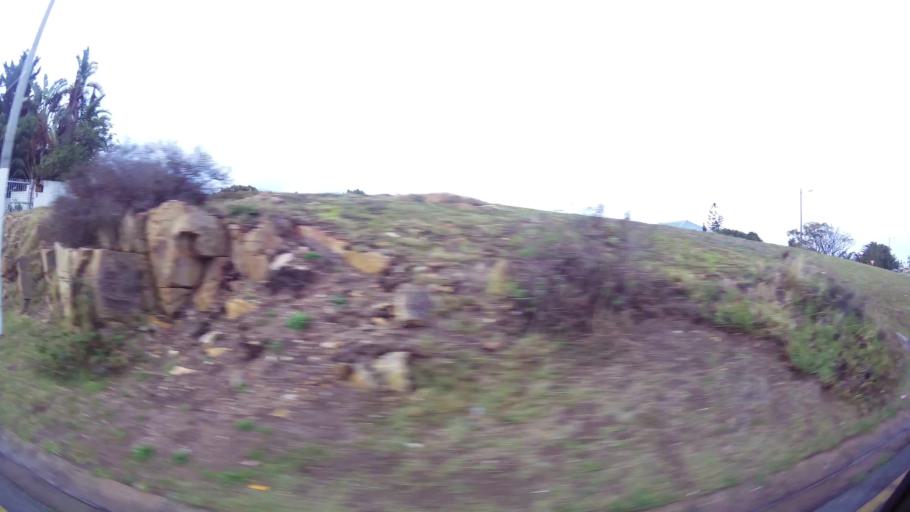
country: ZA
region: Western Cape
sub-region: Eden District Municipality
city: Mossel Bay
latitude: -34.1813
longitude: 22.1340
